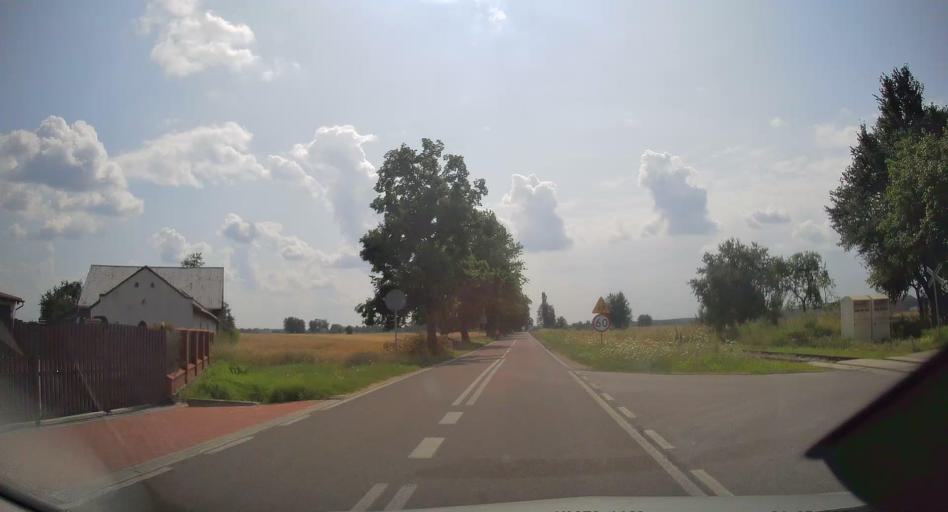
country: PL
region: Lodz Voivodeship
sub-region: Powiat tomaszowski
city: Lubochnia
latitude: 51.5729
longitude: 20.0970
